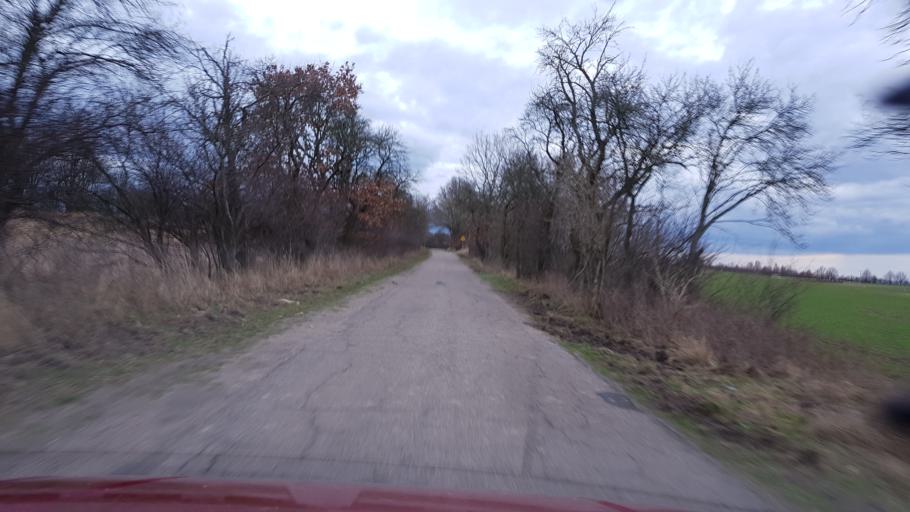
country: PL
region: West Pomeranian Voivodeship
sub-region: Powiat gryfinski
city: Stare Czarnowo
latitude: 53.3300
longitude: 14.6727
